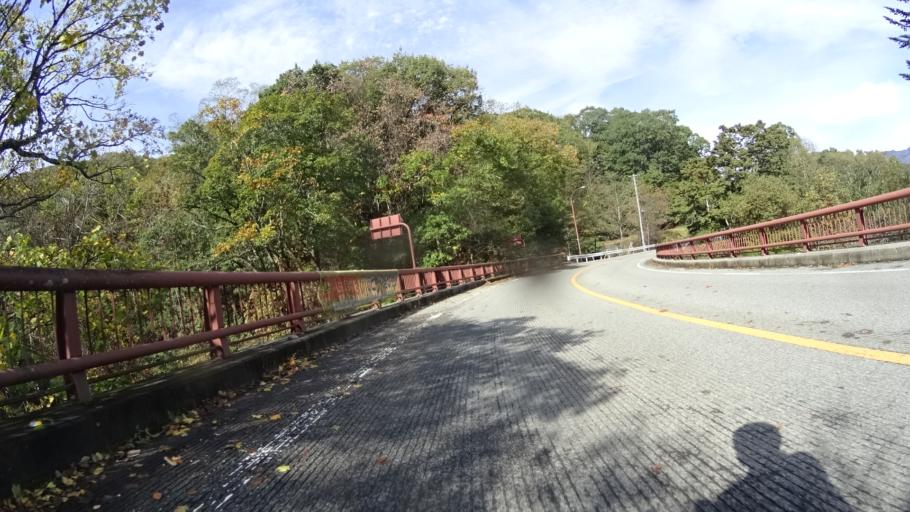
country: JP
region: Yamanashi
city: Enzan
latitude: 35.7826
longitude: 138.8014
